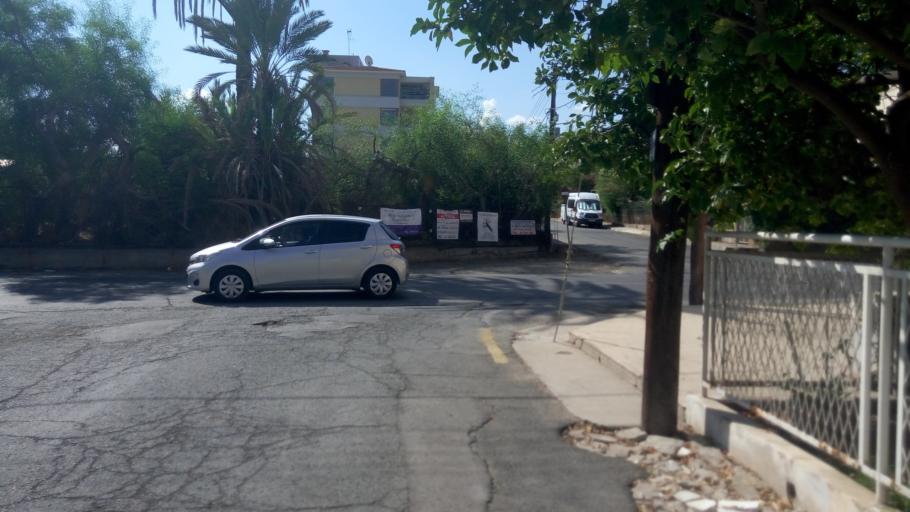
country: CY
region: Lefkosia
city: Nicosia
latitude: 35.1703
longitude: 33.3400
